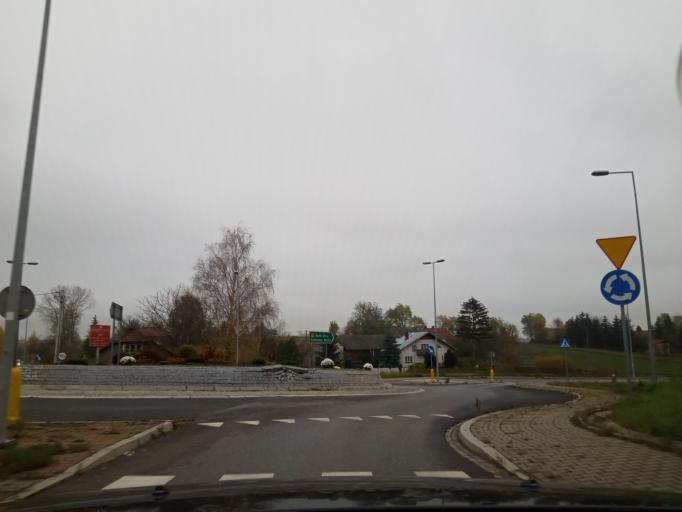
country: PL
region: Lesser Poland Voivodeship
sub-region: Powiat proszowicki
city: Klimontow
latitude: 50.2290
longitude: 20.3195
